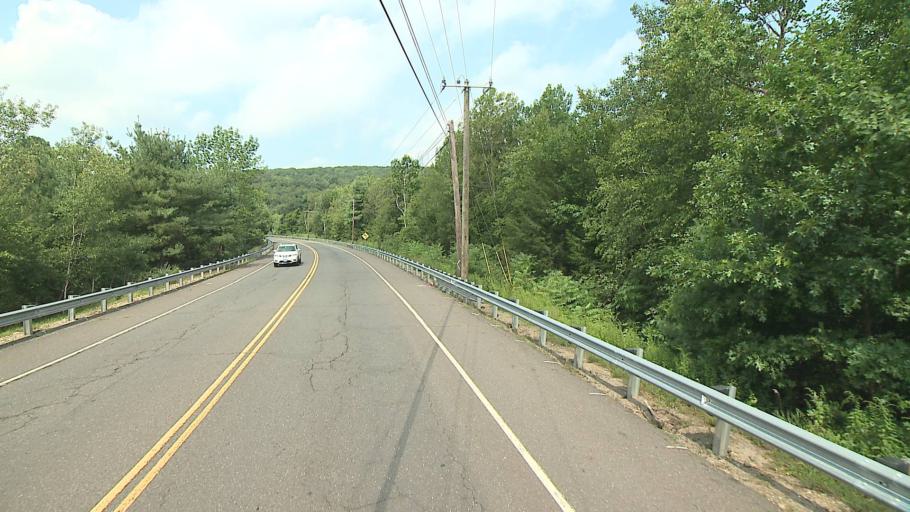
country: US
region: Connecticut
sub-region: Litchfield County
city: Thomaston
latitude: 41.6622
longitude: -73.1088
